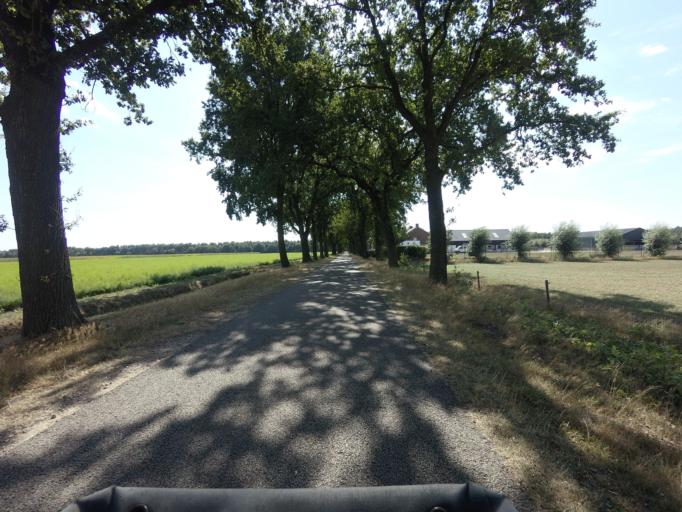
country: NL
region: North Brabant
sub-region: Gemeente Someren
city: Someren
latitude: 51.3451
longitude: 5.6661
